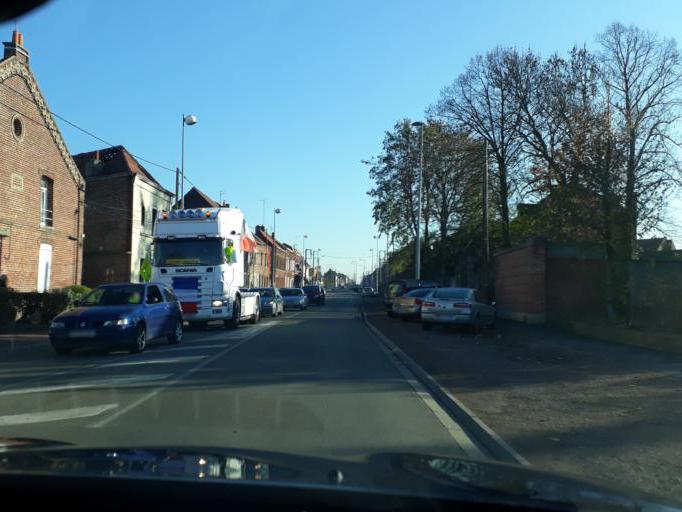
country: FR
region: Nord-Pas-de-Calais
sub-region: Departement du Nord
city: Auberchicourt
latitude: 50.3312
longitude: 3.2409
